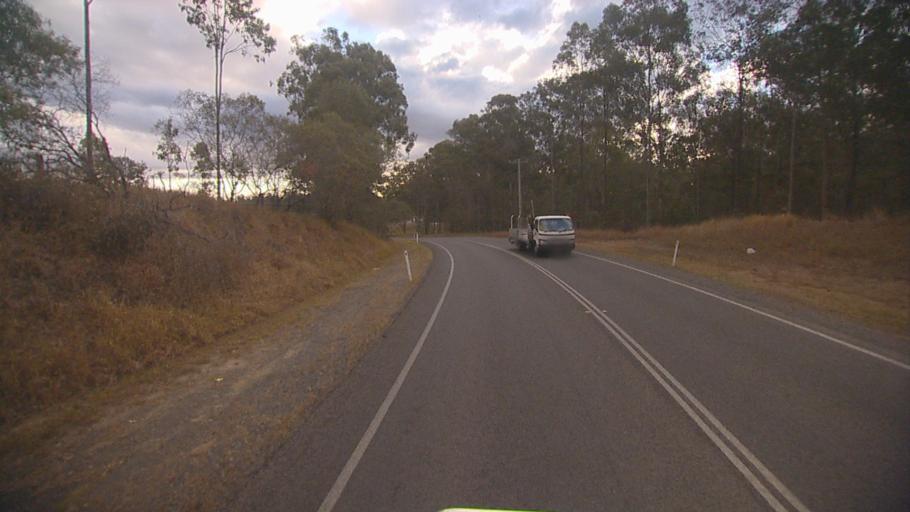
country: AU
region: Queensland
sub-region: Logan
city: Cedar Vale
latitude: -27.8675
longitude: 153.0630
